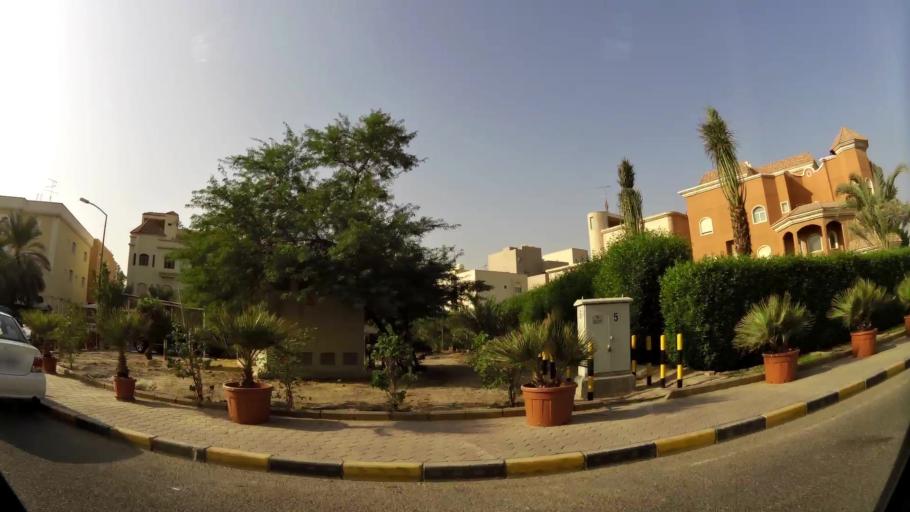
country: KW
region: Al Asimah
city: Ad Dasmah
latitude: 29.3669
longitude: 48.0049
